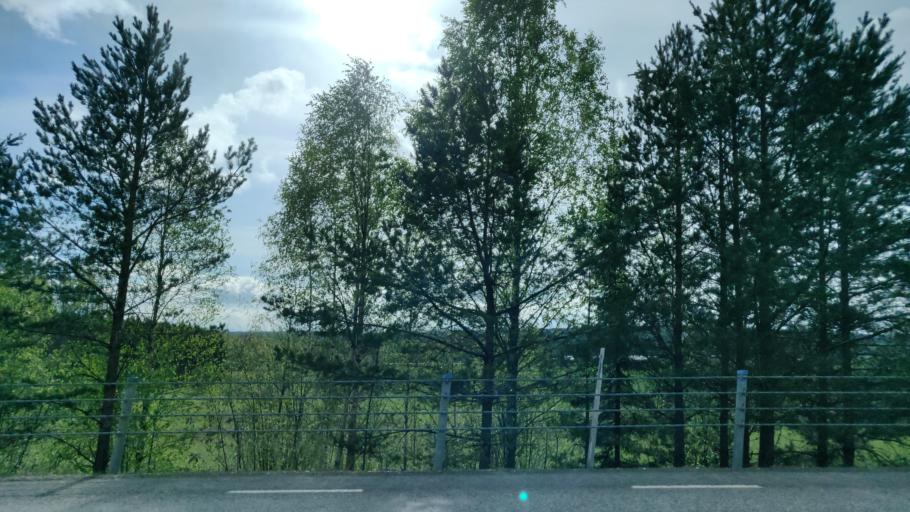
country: SE
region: Vaermland
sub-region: Forshaga Kommun
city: Deje
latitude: 59.5864
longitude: 13.4599
